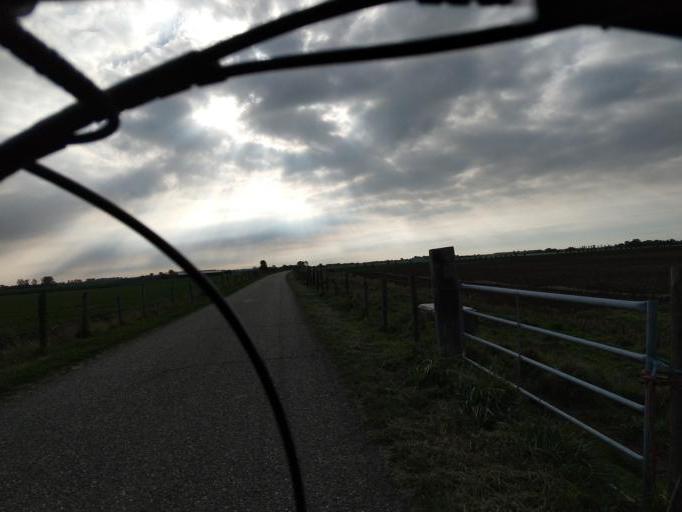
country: NL
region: South Holland
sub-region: Gemeente Goeree-Overflakkee
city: Goedereede
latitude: 51.7124
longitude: 3.9742
